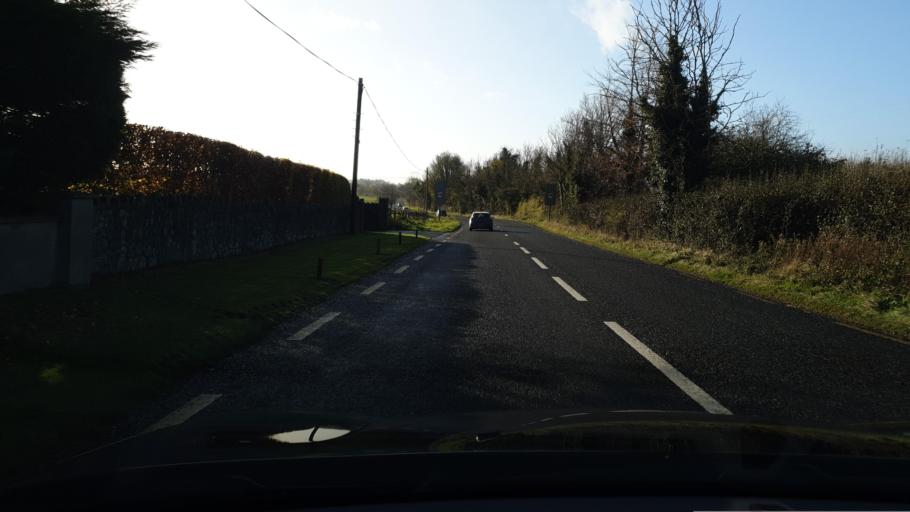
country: IE
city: Confey
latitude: 53.4033
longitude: -6.5277
